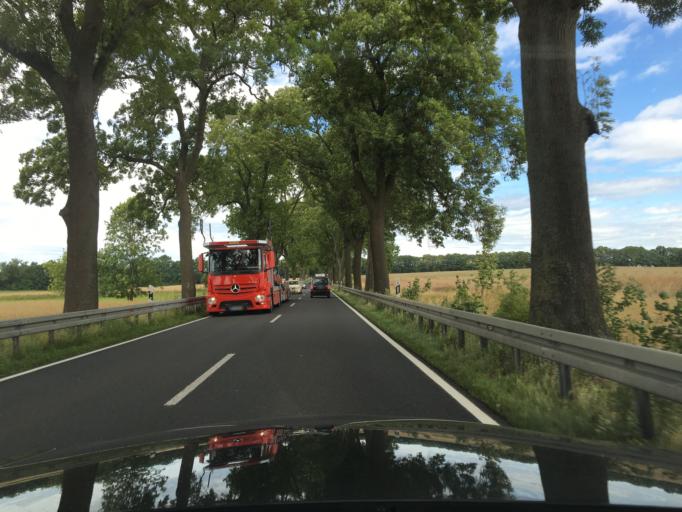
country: DE
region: Brandenburg
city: Gransee
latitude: 52.9567
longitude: 13.1505
